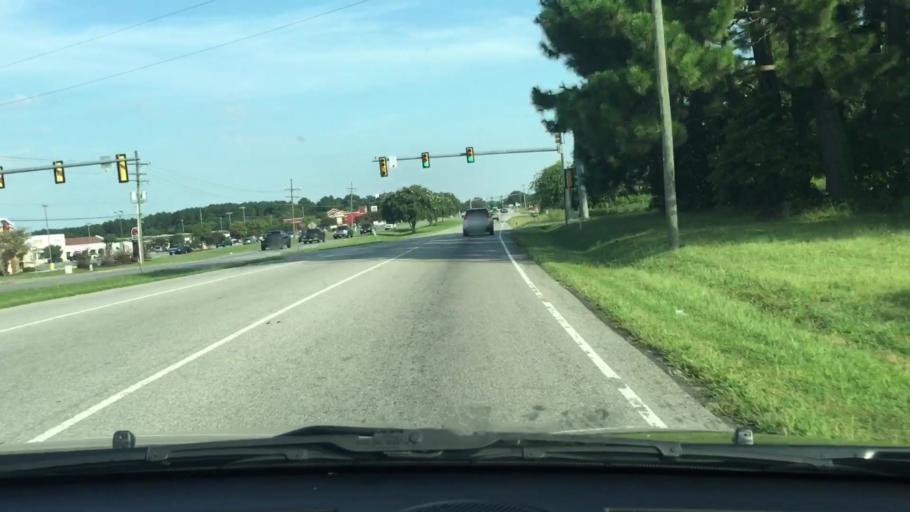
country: US
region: Virginia
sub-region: Isle of Wight County
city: Carrollton
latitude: 36.9542
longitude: -76.6007
